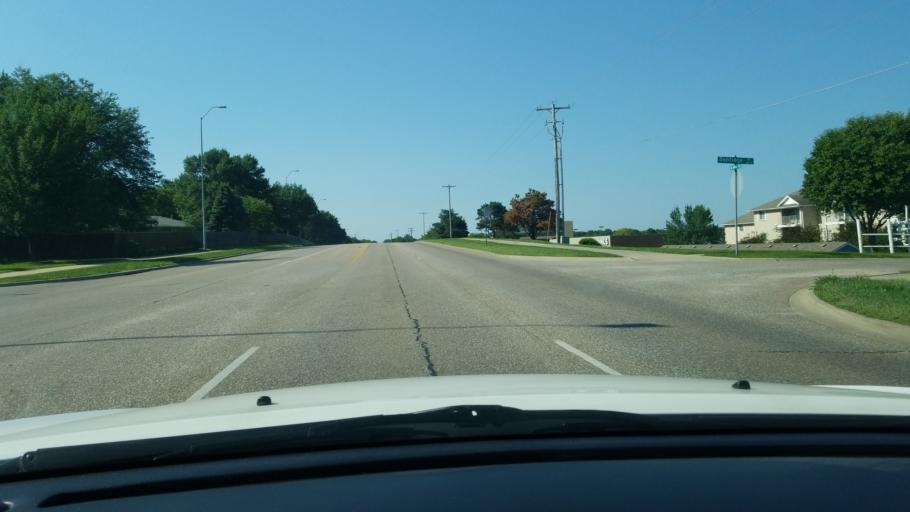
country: US
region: Nebraska
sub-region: Lancaster County
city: Lincoln
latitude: 40.8188
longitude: -96.6060
